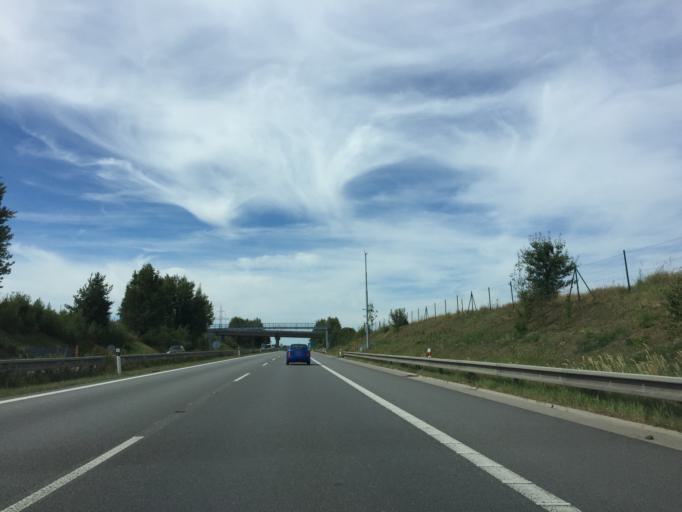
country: CZ
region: Jihocesky
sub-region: Okres Tabor
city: Sezimovo Usti
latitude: 49.4206
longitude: 14.7045
